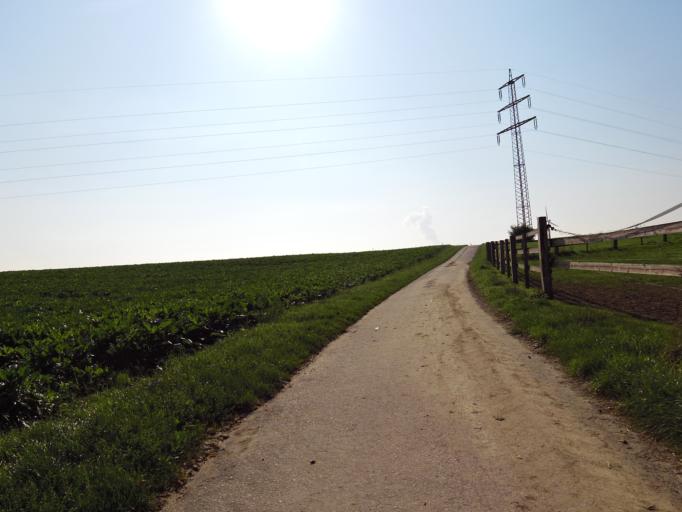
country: DE
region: North Rhine-Westphalia
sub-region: Regierungsbezirk Koln
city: Ubach-Palenberg
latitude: 50.9418
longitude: 6.1391
